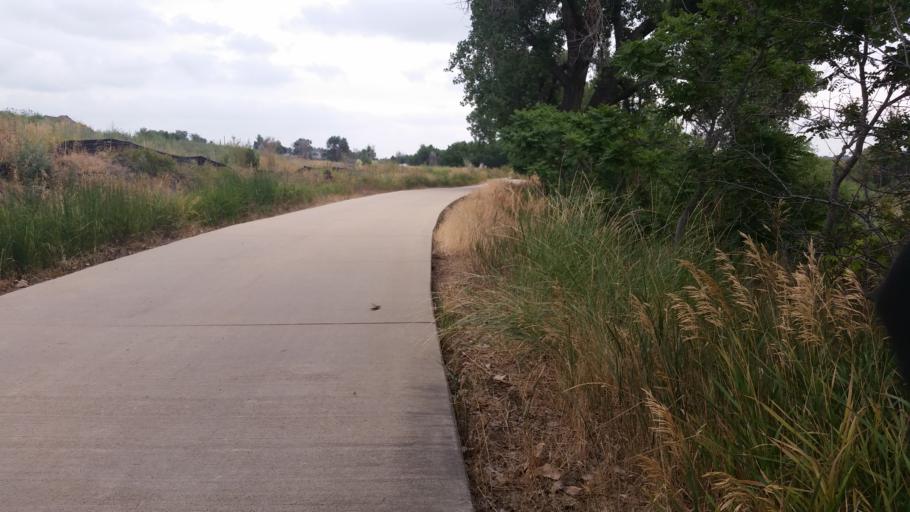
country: US
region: Colorado
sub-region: Adams County
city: Twin Lakes
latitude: 39.8176
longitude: -104.9999
